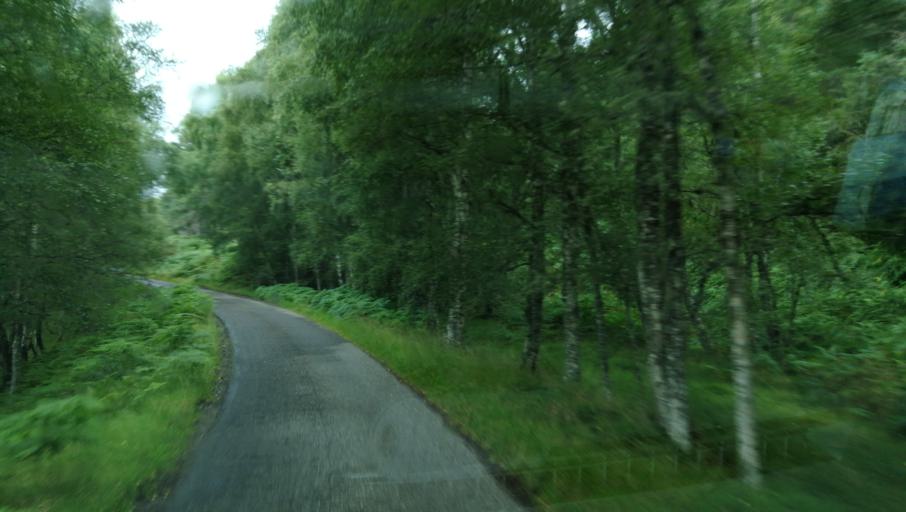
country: GB
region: Scotland
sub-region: Highland
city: Spean Bridge
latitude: 57.3016
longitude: -4.8868
